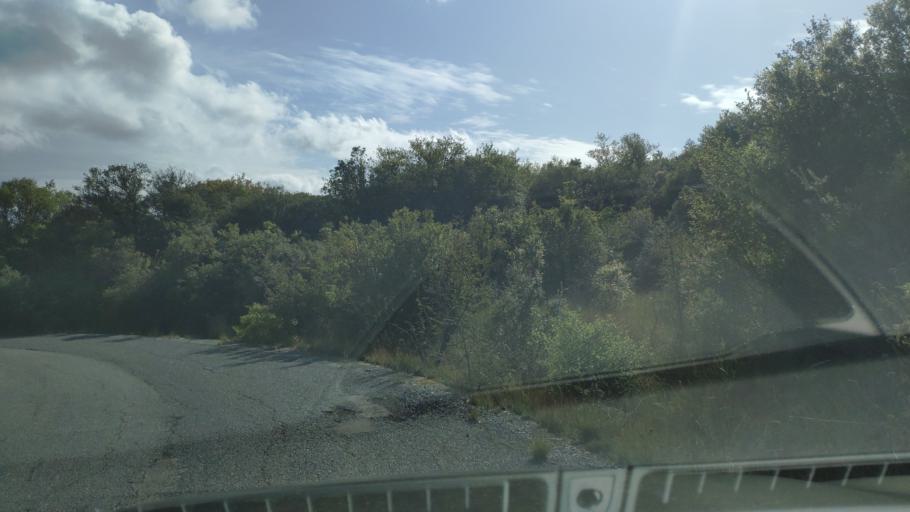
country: GR
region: Peloponnese
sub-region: Nomos Arkadias
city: Dimitsana
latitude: 37.5699
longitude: 22.0063
